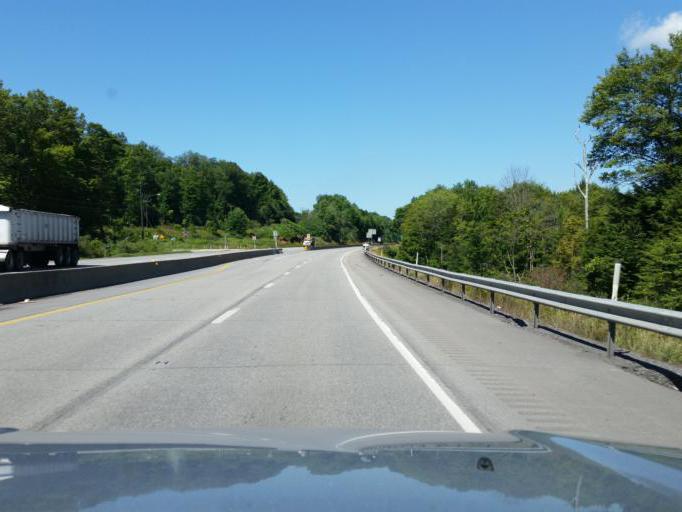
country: US
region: Pennsylvania
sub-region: Cambria County
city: Mundys Corner
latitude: 40.4467
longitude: -78.8013
